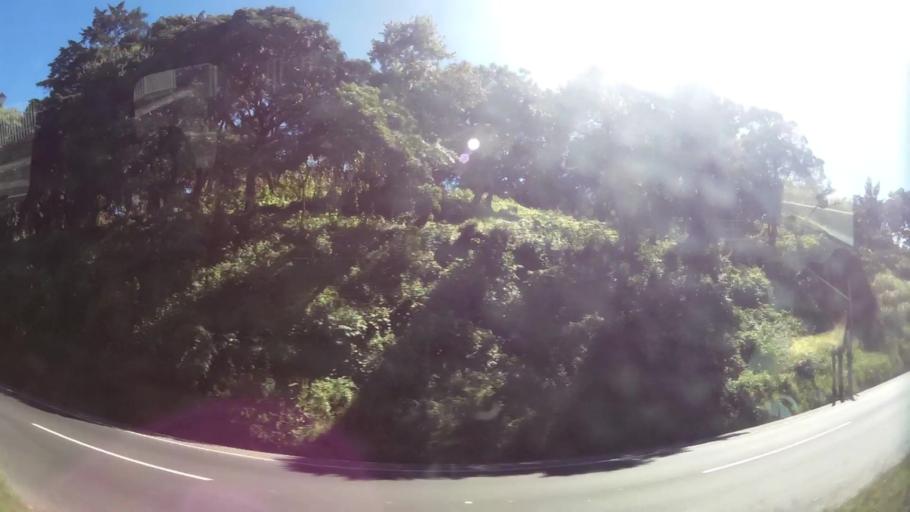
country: GT
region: Guatemala
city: Santa Catarina Pinula
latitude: 14.5341
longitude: -90.4601
